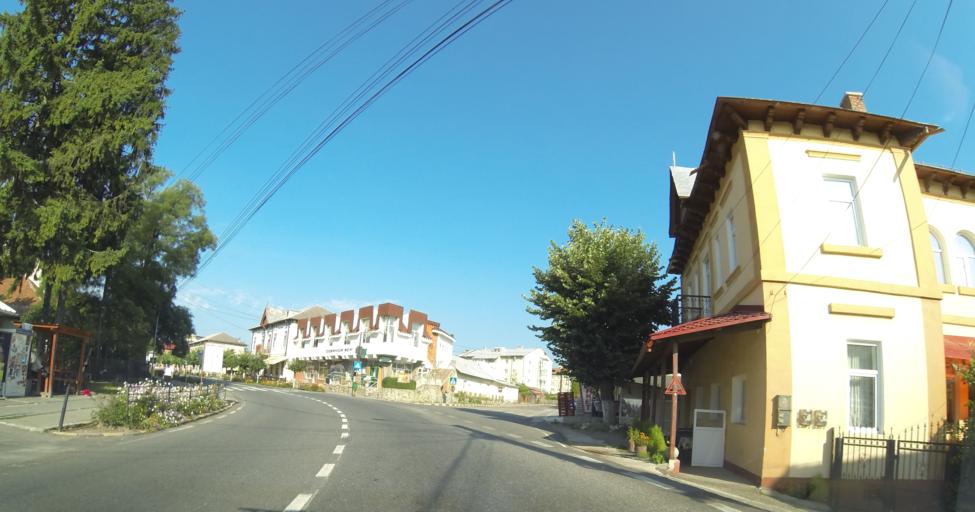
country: RO
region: Valcea
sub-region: Comuna Horezu
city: Horezu
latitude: 45.1459
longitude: 23.9934
